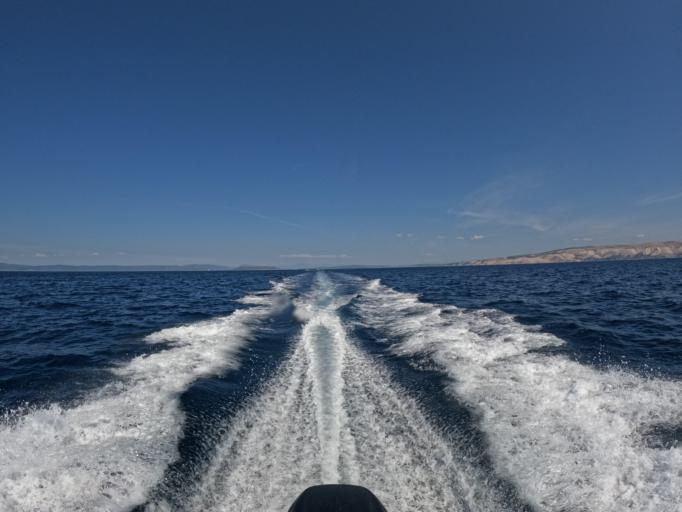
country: HR
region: Primorsko-Goranska
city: Lopar
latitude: 44.8900
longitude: 14.6456
